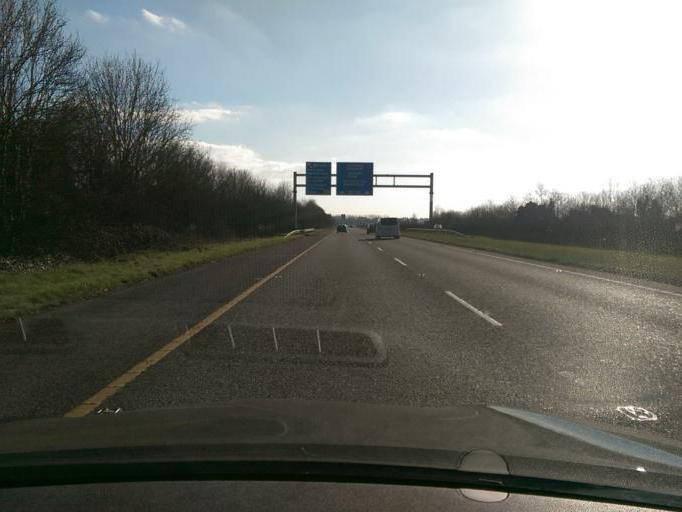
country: IE
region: Leinster
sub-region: Kildare
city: Kilcullen
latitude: 53.1811
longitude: -6.7382
